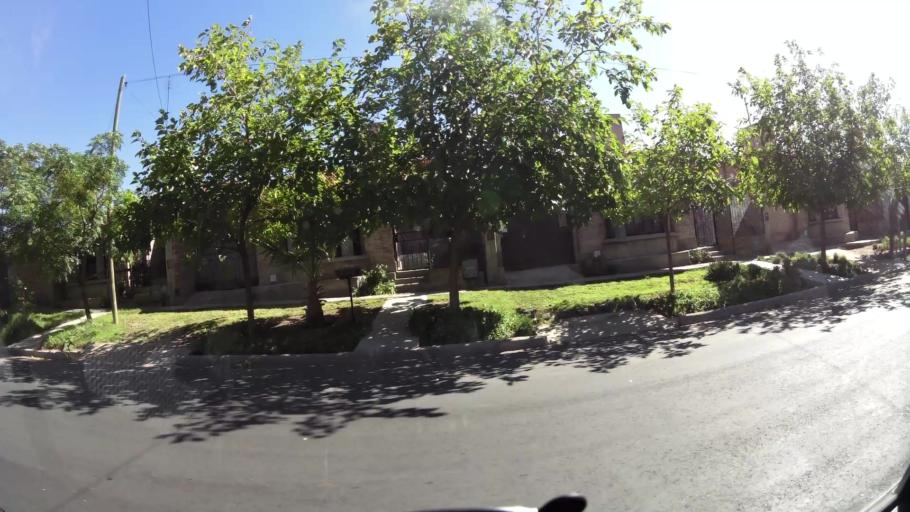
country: AR
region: Mendoza
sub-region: Departamento de Godoy Cruz
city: Godoy Cruz
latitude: -32.9121
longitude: -68.8805
